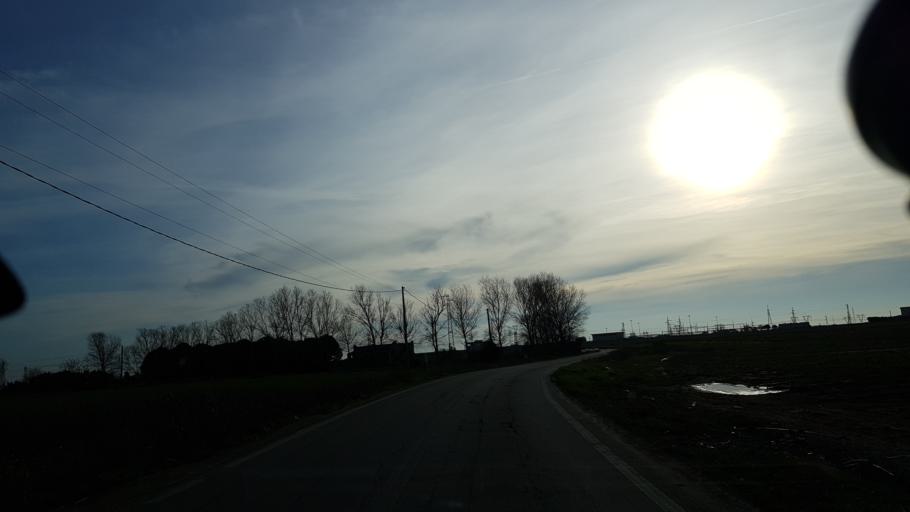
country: IT
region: Apulia
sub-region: Provincia di Brindisi
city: Brindisi
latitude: 40.6092
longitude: 17.9128
